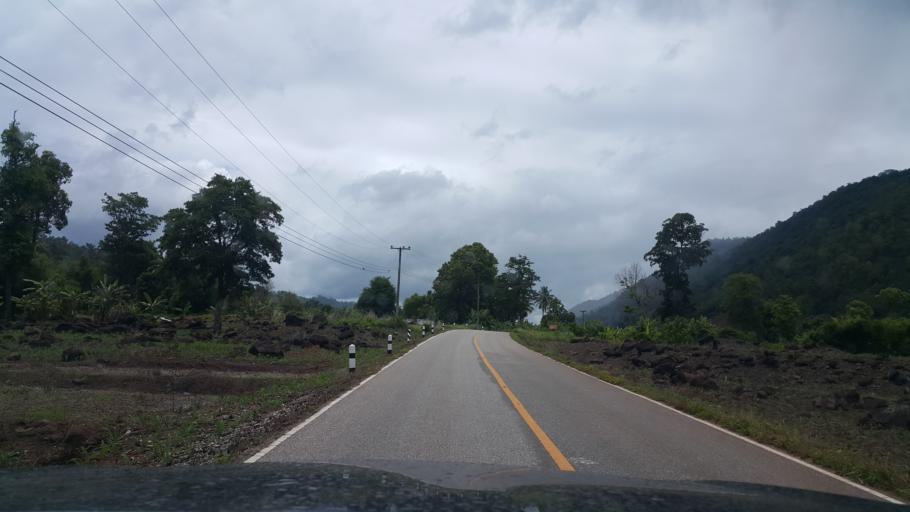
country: TH
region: Loei
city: Na Haeo
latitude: 17.5466
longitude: 100.8399
